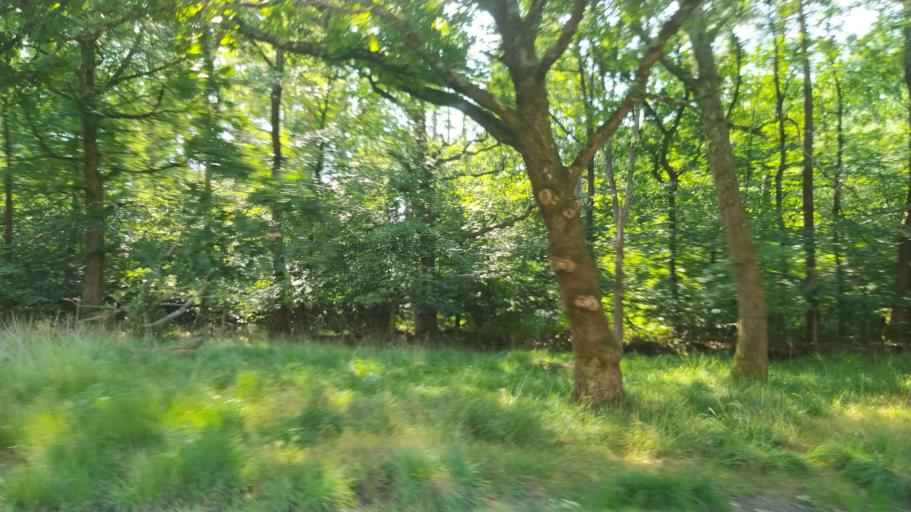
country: GB
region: England
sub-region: Hampshire
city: Totton
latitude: 50.8954
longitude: -1.5333
